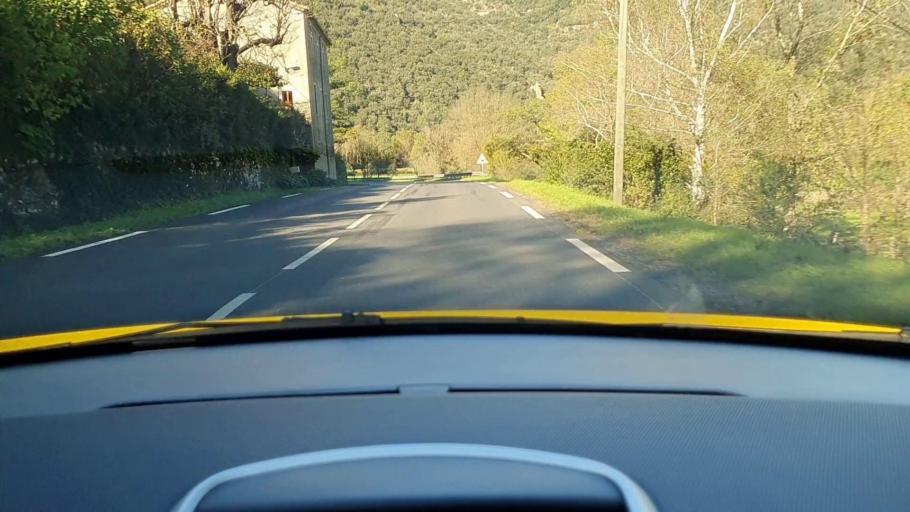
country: FR
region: Languedoc-Roussillon
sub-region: Departement du Gard
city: Sumene
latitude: 44.0153
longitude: 3.6793
